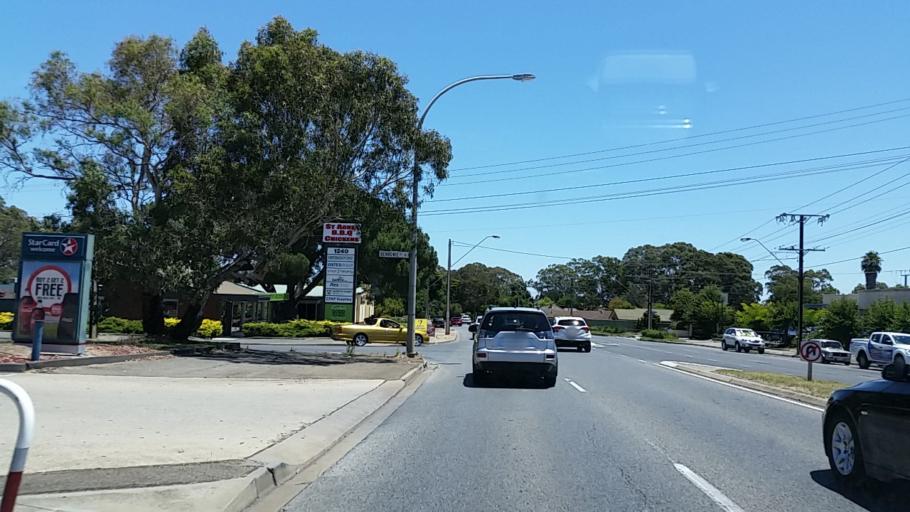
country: AU
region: South Australia
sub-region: Tea Tree Gully
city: Hope Valley
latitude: -34.8212
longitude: 138.7156
